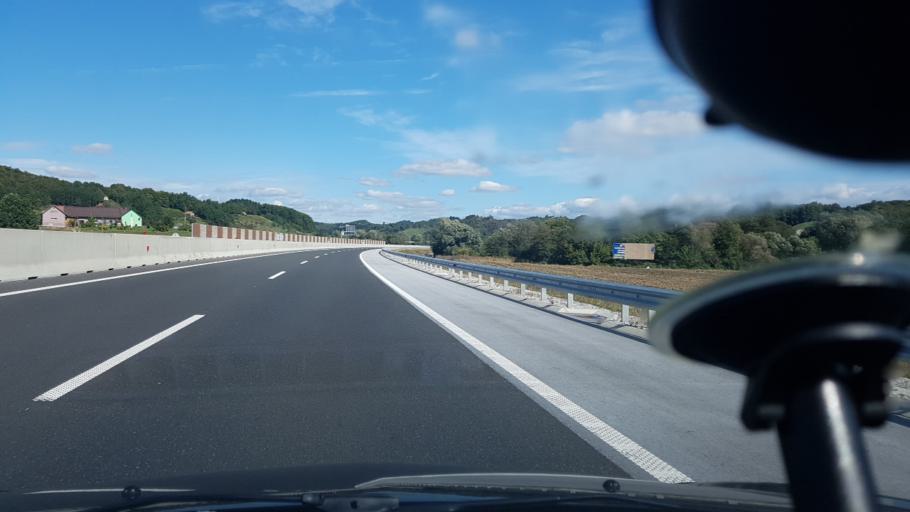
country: SI
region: Podlehnik
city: Podlehnik
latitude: 46.3123
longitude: 15.8685
